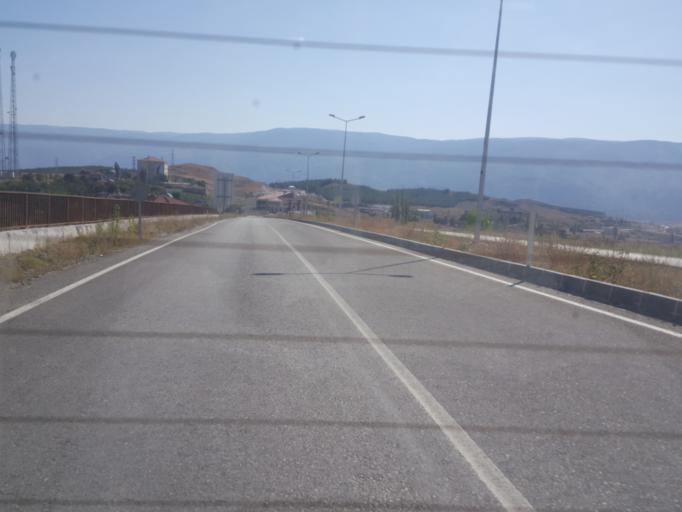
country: TR
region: Kastamonu
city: Tosya
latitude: 41.0073
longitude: 34.0602
